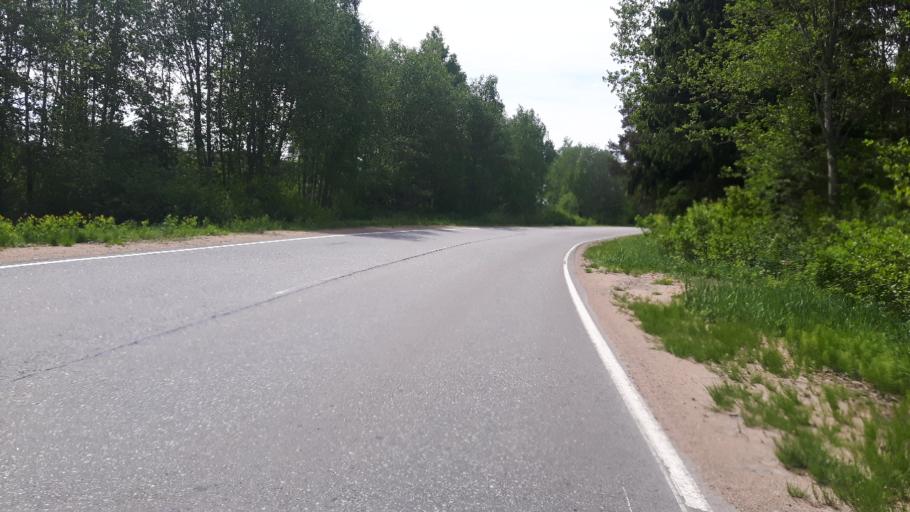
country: RU
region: Leningrad
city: Ust'-Luga
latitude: 59.6509
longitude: 28.2370
